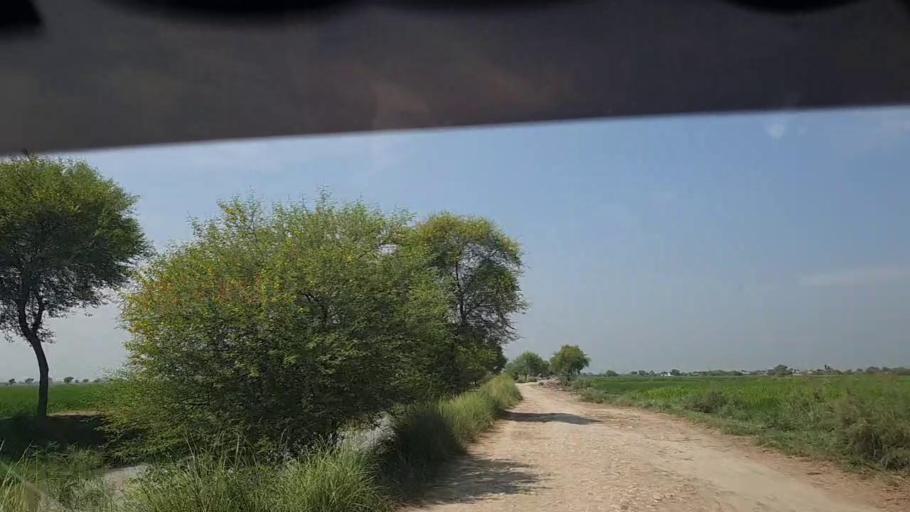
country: PK
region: Sindh
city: Thul
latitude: 28.1836
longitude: 68.7229
